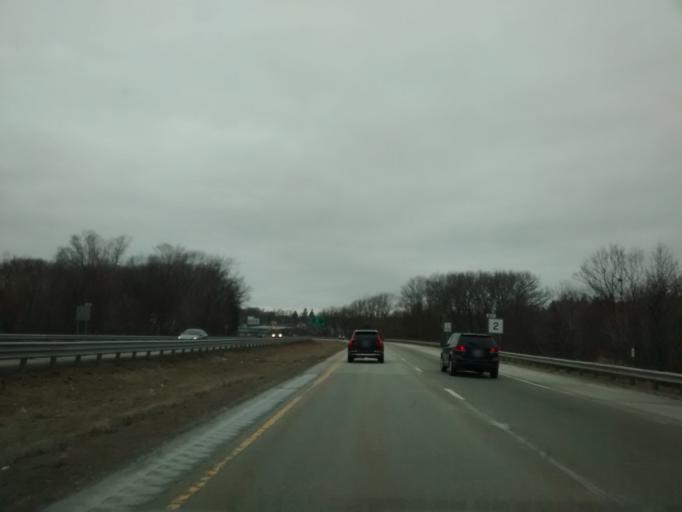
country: US
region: Massachusetts
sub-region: Worcester County
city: Gardner
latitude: 42.5665
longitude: -71.9847
